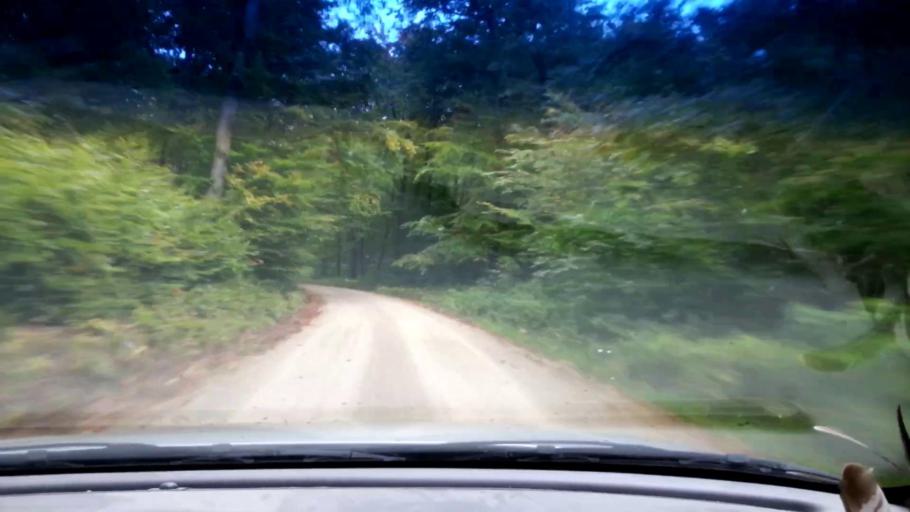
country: DE
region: Bavaria
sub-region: Upper Franconia
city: Litzendorf
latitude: 49.8959
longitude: 11.0627
